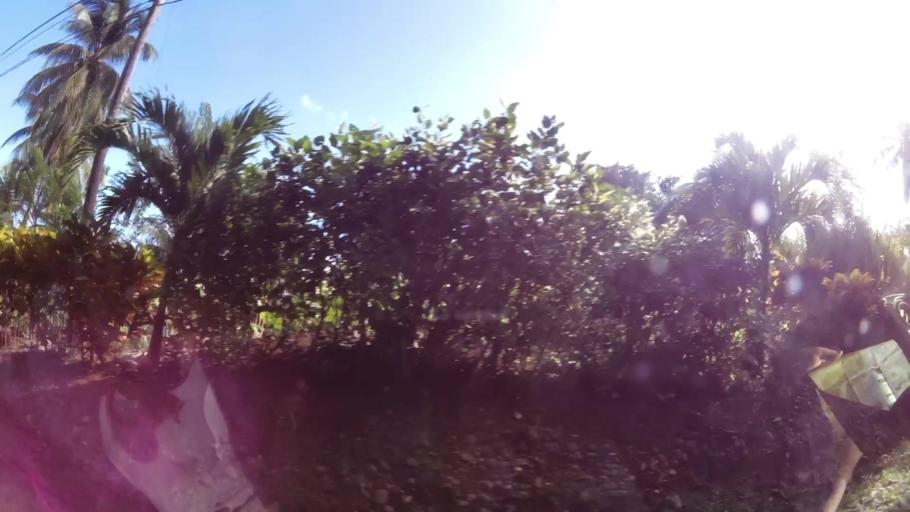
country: DM
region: Saint Andrew
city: Marigot
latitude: 15.5174
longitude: -61.2651
